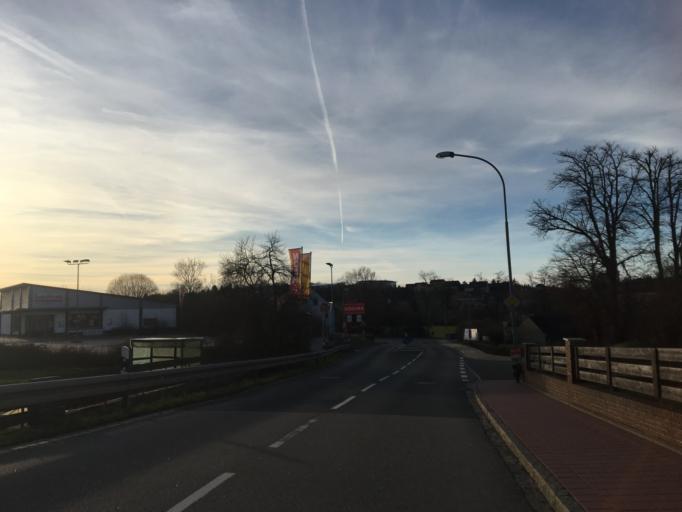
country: DE
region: Bavaria
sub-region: Regierungsbezirk Mittelfranken
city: Wilhermsdorf
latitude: 49.4780
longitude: 10.7196
